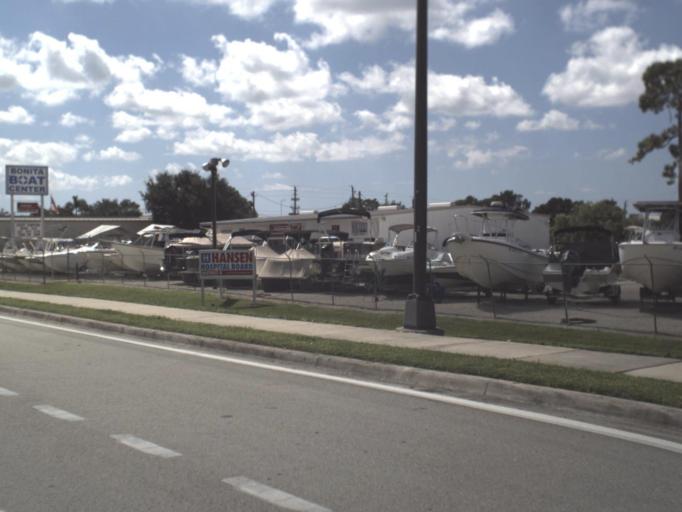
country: US
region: Florida
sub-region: Lee County
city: Bonita Springs
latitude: 26.3358
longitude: -81.8065
